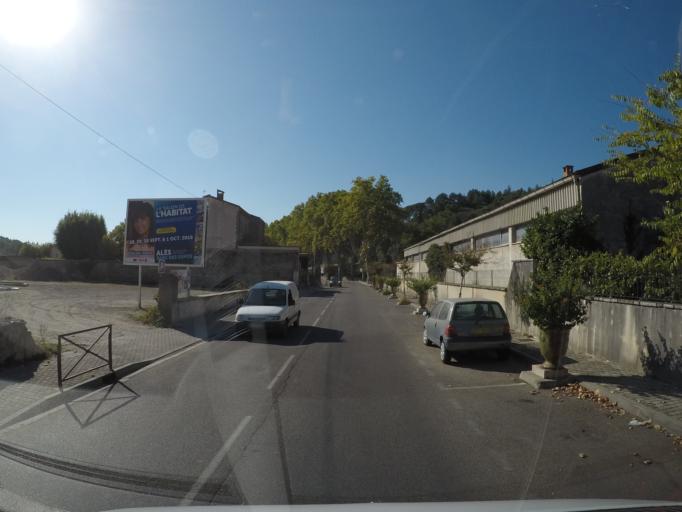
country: FR
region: Languedoc-Roussillon
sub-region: Departement du Gard
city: Anduze
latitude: 44.0505
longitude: 3.9852
